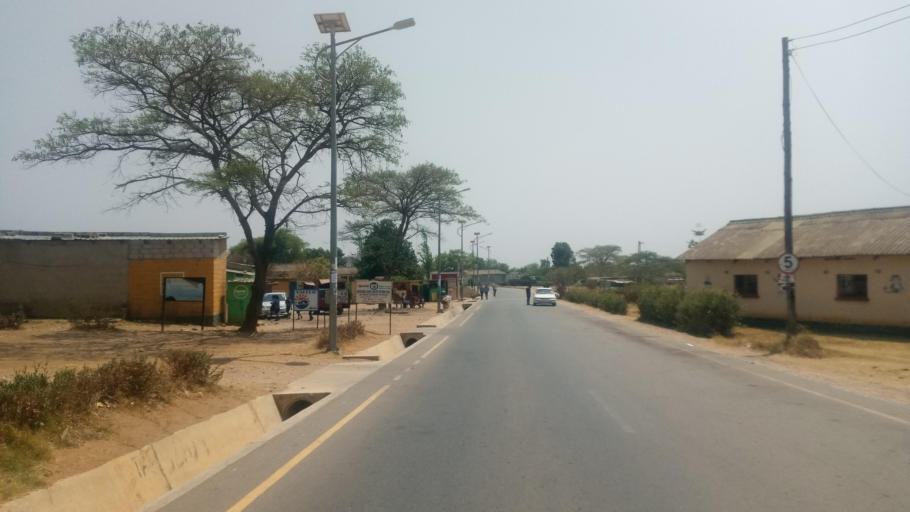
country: ZM
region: Lusaka
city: Lusaka
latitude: -15.4498
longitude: 28.4417
